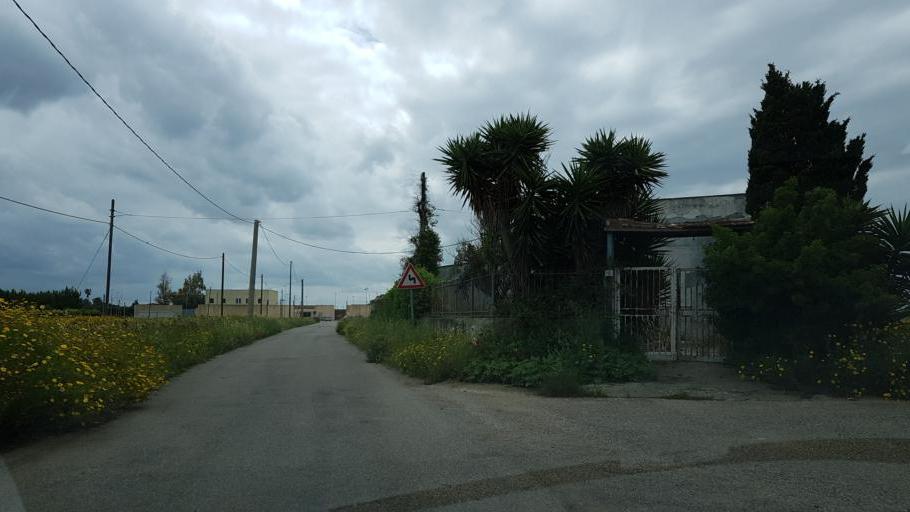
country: IT
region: Apulia
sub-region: Provincia di Brindisi
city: Brindisi
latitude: 40.6342
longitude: 17.8704
